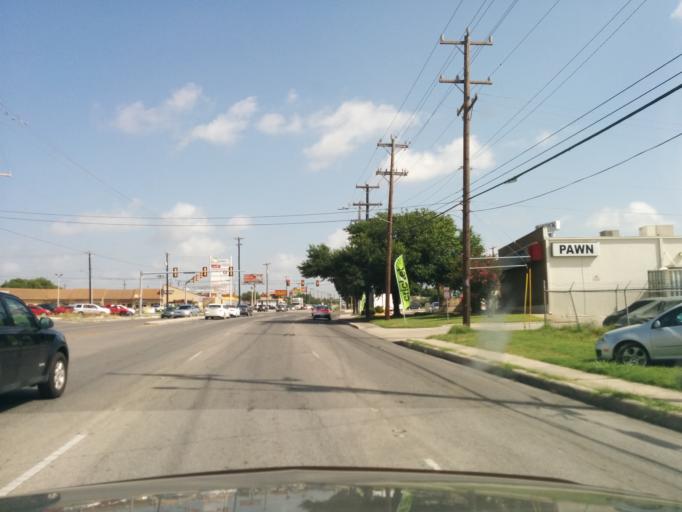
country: US
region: Texas
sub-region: Bexar County
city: Leon Valley
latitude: 29.5229
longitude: -98.5993
